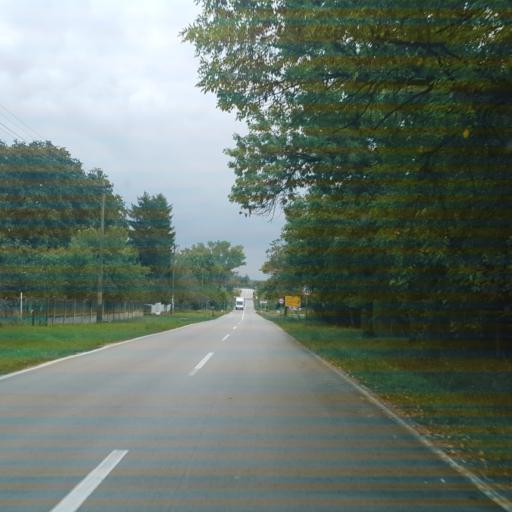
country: RS
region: Central Serbia
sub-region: Nisavski Okrug
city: Razanj
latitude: 43.6198
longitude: 21.5800
